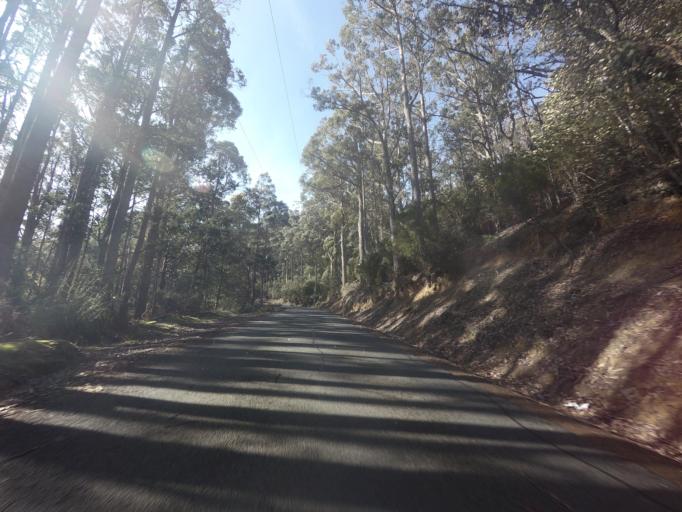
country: AU
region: Tasmania
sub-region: Kingborough
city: Kettering
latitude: -43.1694
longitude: 147.1823
